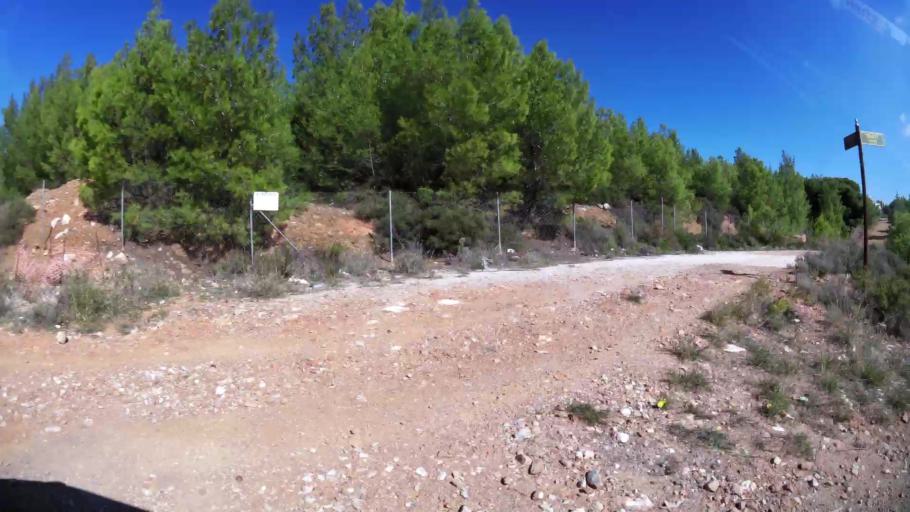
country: GR
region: Attica
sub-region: Nomarchia Anatolikis Attikis
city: Dioni
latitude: 38.0269
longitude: 23.9267
